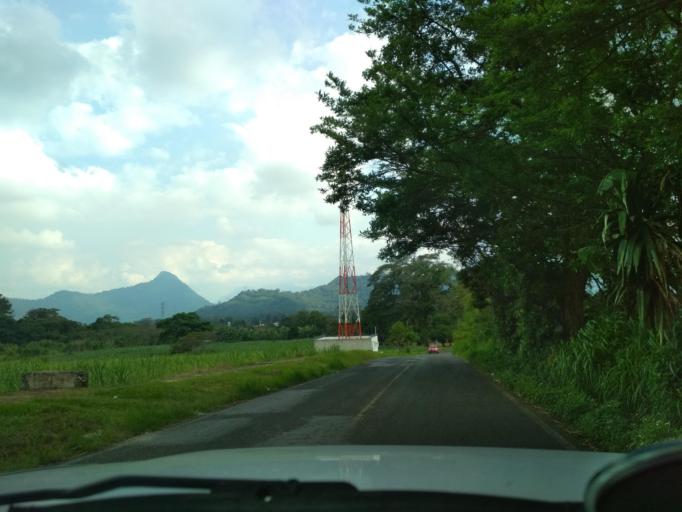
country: MX
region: Veracruz
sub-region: Fortin
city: Monte Salas
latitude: 18.9167
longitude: -97.0260
